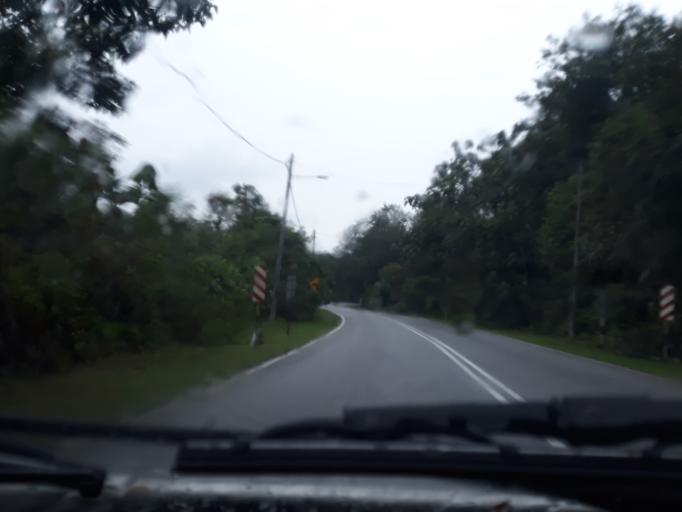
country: MY
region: Kedah
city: Kulim
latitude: 5.2771
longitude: 100.6189
